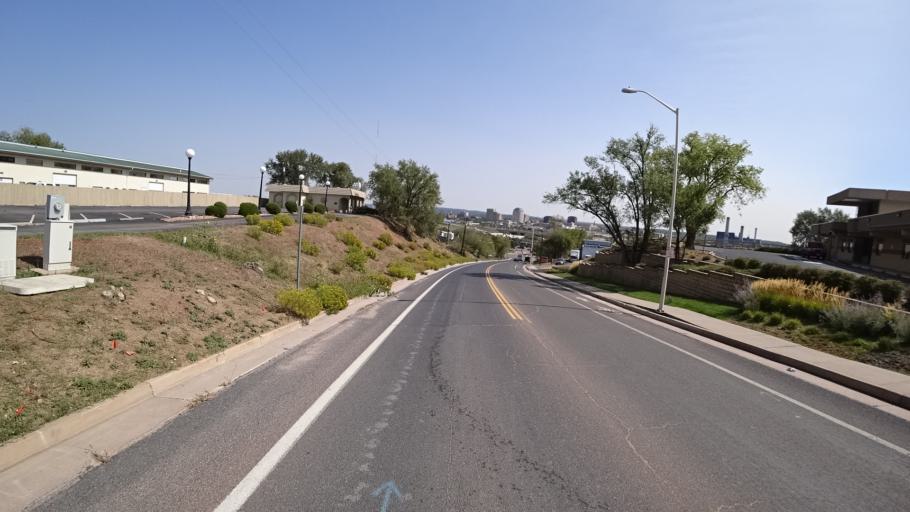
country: US
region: Colorado
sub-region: El Paso County
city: Colorado Springs
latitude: 38.8252
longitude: -104.8428
